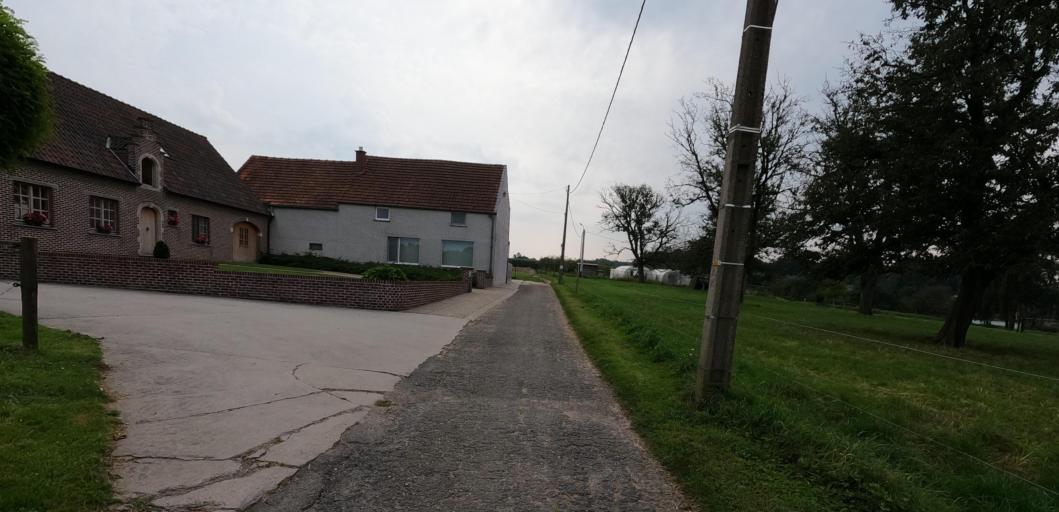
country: BE
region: Flanders
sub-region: Provincie Vlaams-Brabant
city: Merchtem
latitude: 50.9444
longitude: 4.2520
